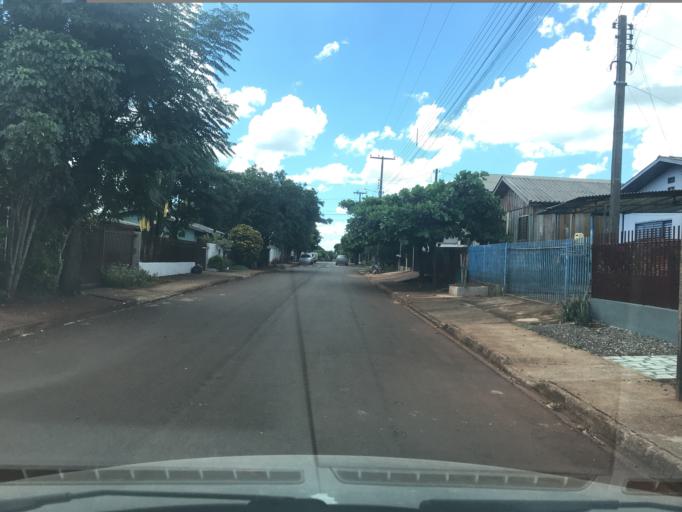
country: BR
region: Parana
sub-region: Palotina
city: Palotina
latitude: -24.2746
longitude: -53.8476
